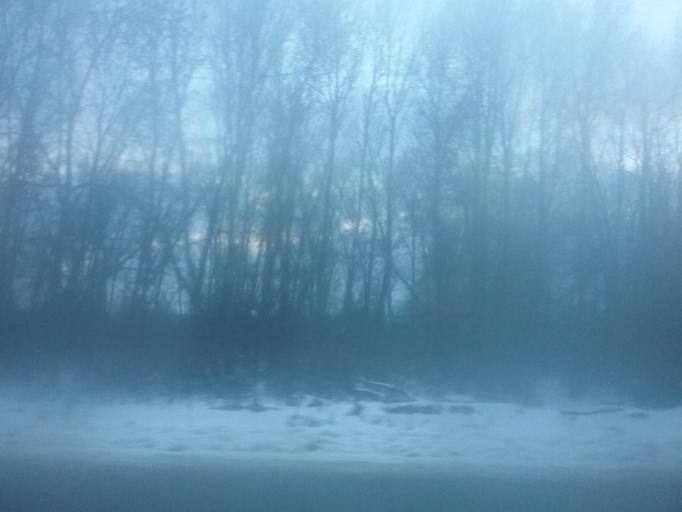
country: RU
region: Tula
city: Kireyevsk
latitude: 54.0197
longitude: 37.9208
